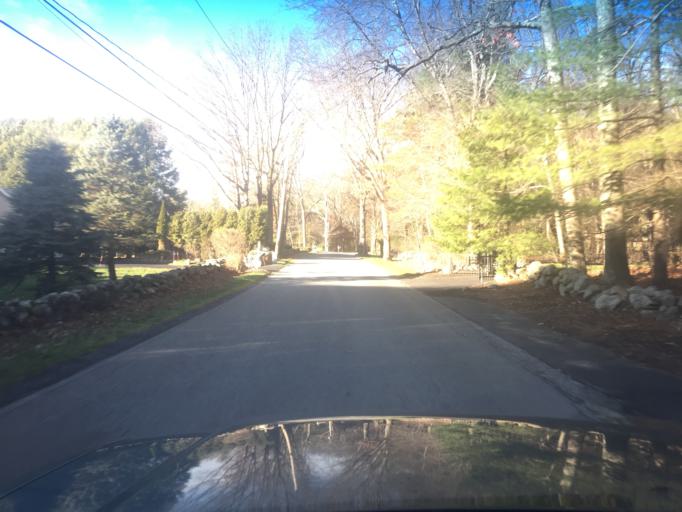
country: US
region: Massachusetts
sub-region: Middlesex County
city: Holliston
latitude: 42.2111
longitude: -71.4622
